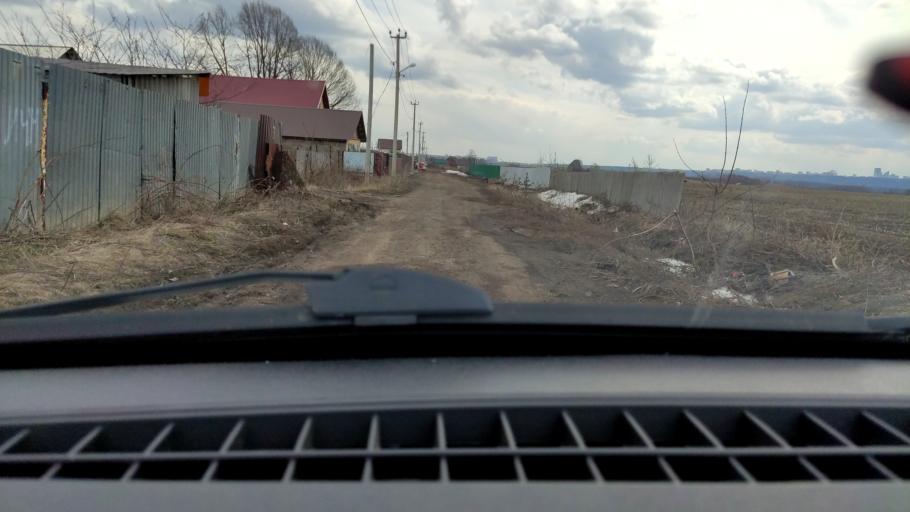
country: RU
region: Bashkortostan
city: Mikhaylovka
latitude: 54.8338
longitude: 55.9510
